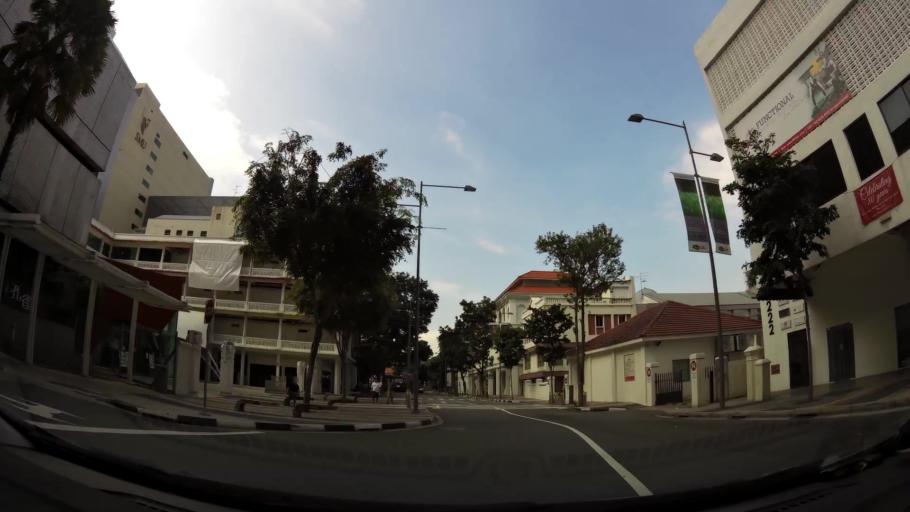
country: SG
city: Singapore
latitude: 1.2977
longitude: 103.8520
